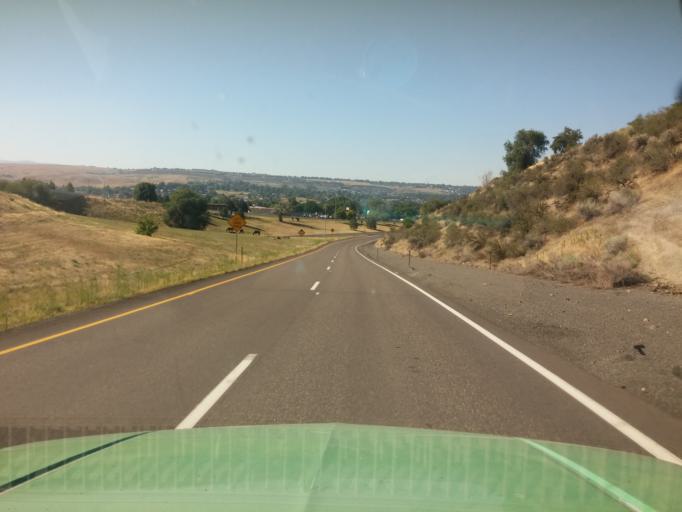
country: US
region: Idaho
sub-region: Nez Perce County
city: Lewiston
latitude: 46.4319
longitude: -116.9957
